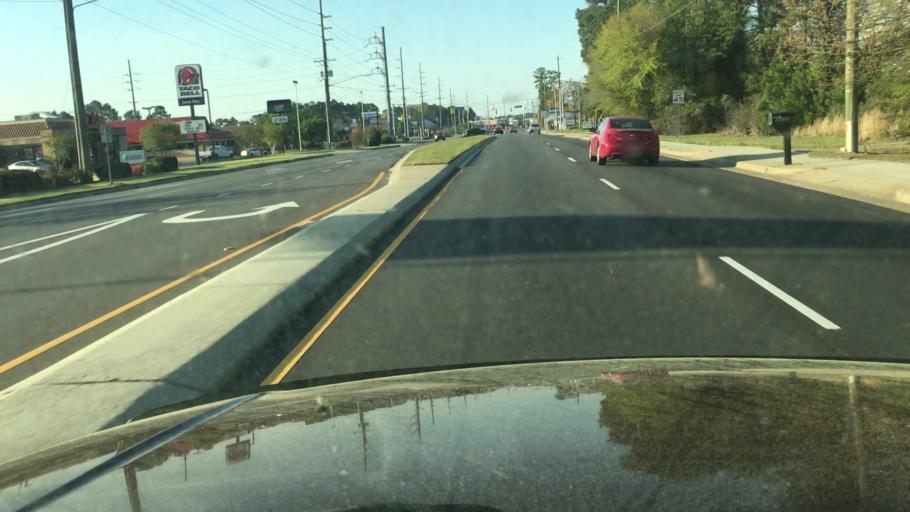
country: US
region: North Carolina
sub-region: Cumberland County
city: Fayetteville
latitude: 35.1241
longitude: -78.8794
